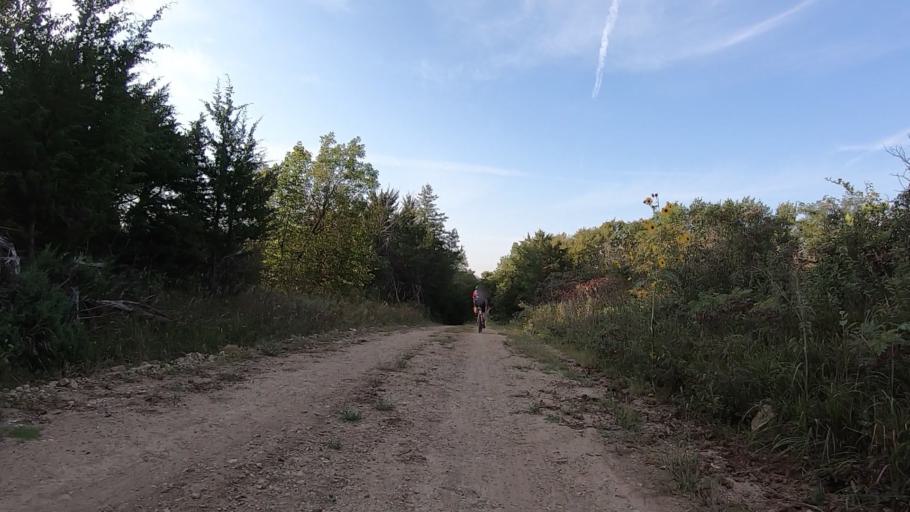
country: US
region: Kansas
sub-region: Marshall County
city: Blue Rapids
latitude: 39.7560
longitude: -96.7506
